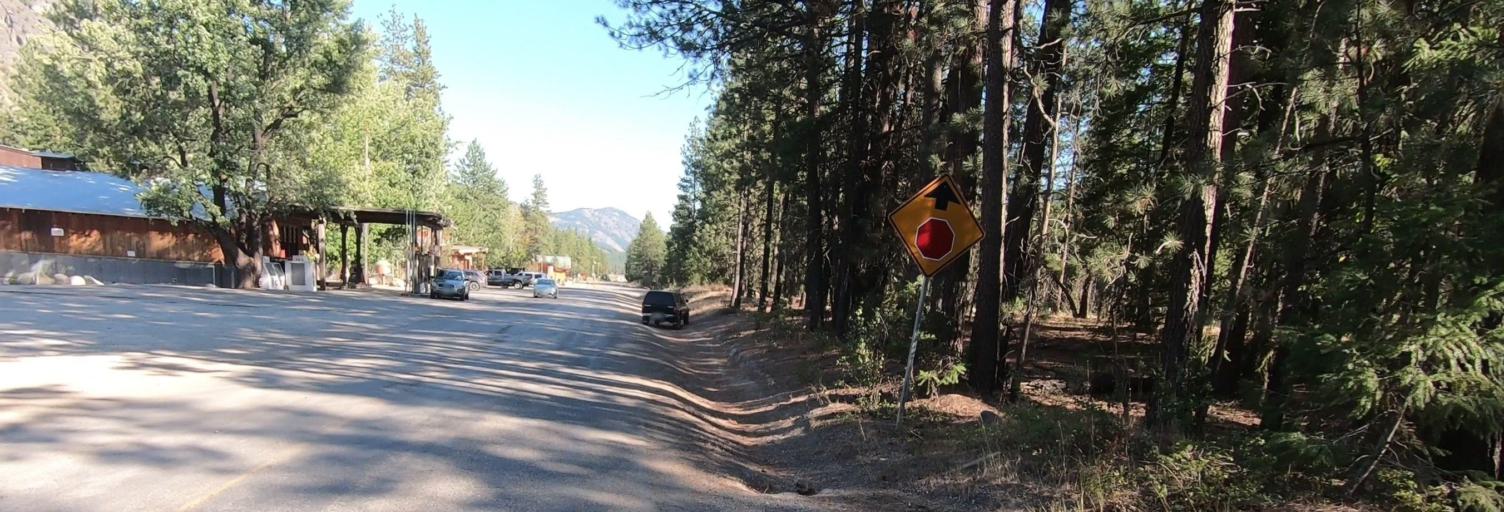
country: US
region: Washington
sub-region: Chelan County
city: Granite Falls
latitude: 48.5936
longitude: -120.4074
